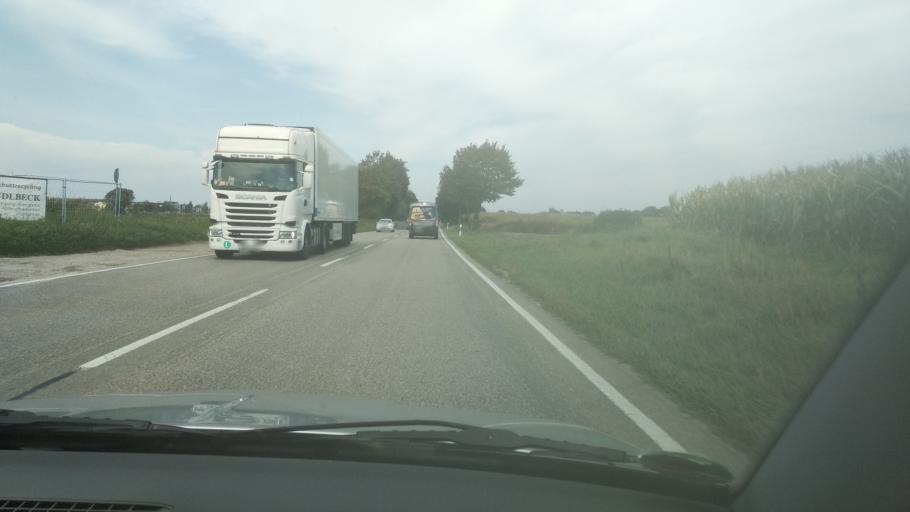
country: DE
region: Bavaria
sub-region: Upper Bavaria
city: Ismaning
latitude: 48.2227
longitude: 11.6897
